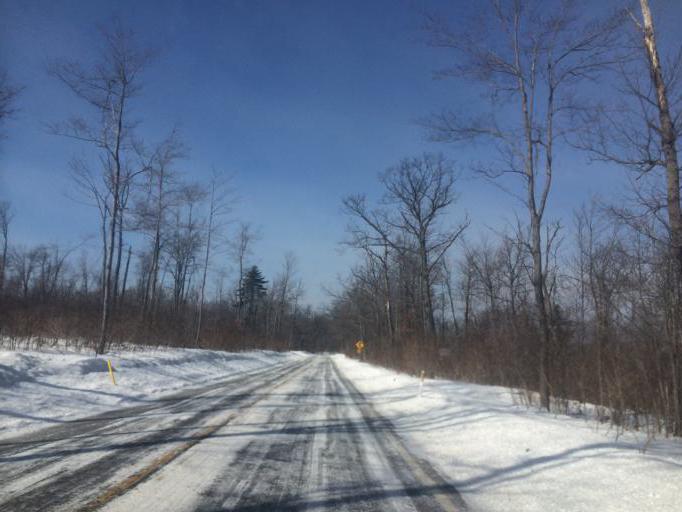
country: US
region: Pennsylvania
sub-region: Centre County
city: Stormstown
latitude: 40.8840
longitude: -78.0237
